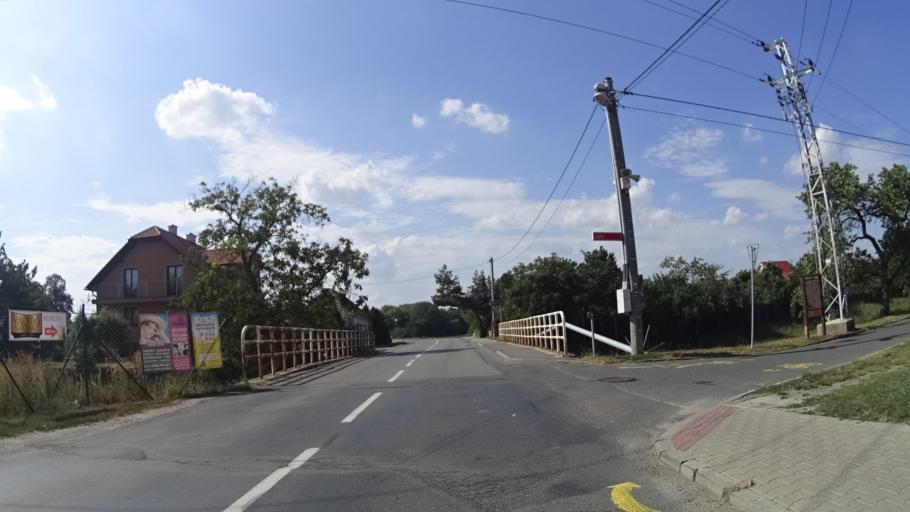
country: CZ
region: Zlin
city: Uhersky Ostroh
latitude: 48.9865
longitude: 17.3944
